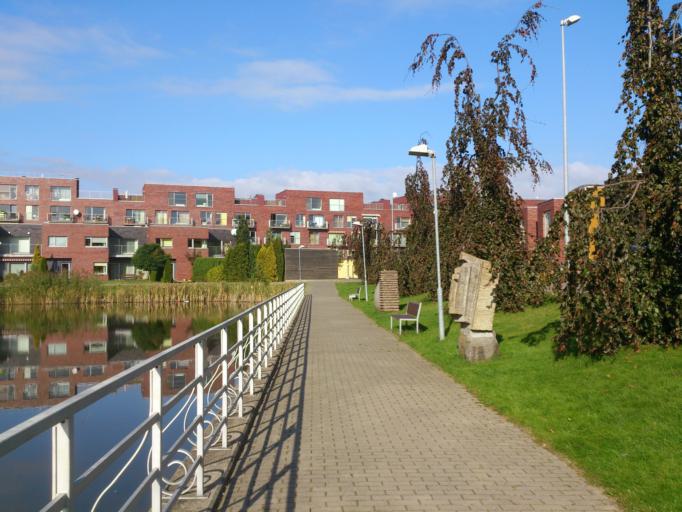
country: LT
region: Kauno apskritis
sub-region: Kaunas
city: Aleksotas
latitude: 54.8738
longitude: 23.9071
